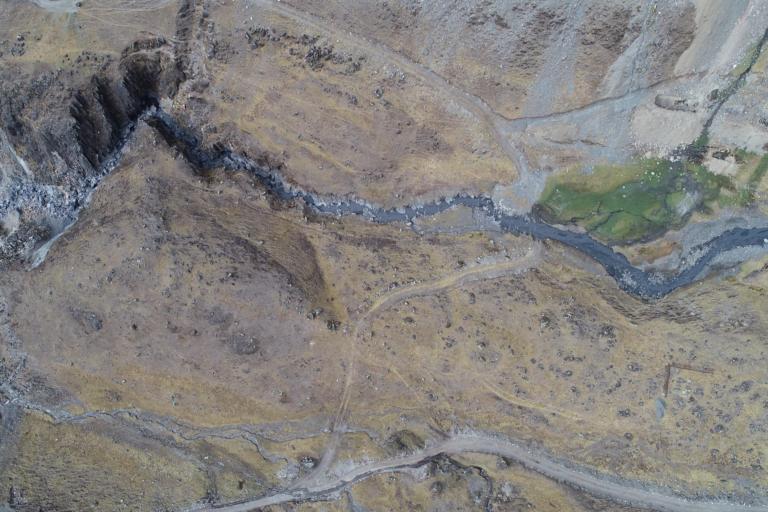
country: BO
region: La Paz
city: Sorata
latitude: -15.6706
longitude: -68.5519
